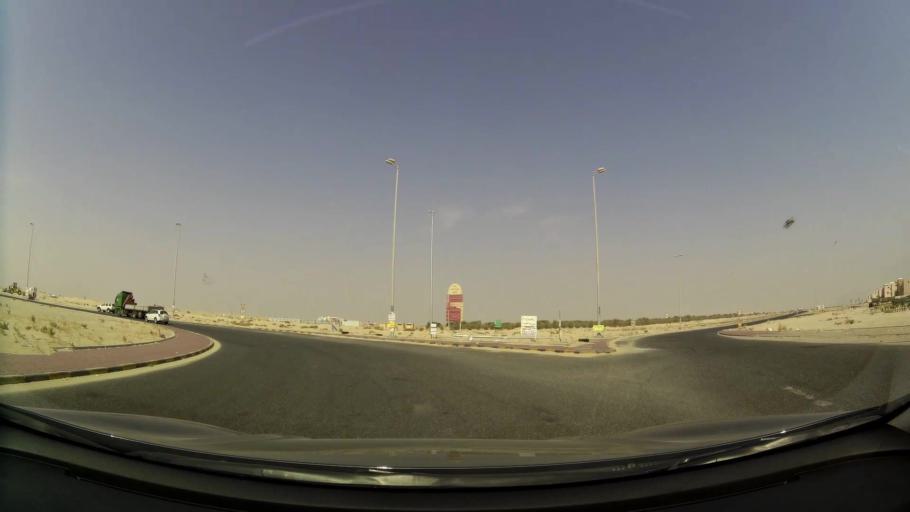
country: KW
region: Al Ahmadi
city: Al Wafrah
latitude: 28.8047
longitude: 48.0451
